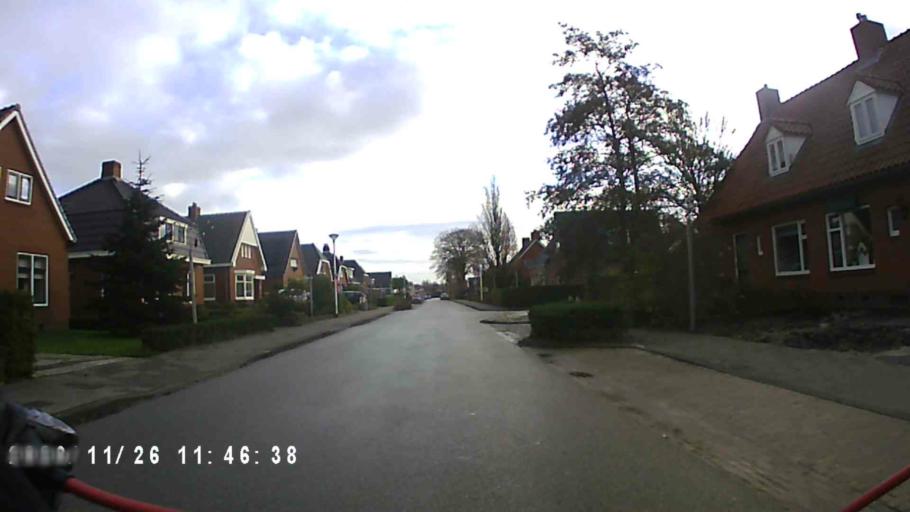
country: NL
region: Groningen
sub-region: Gemeente Bedum
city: Bedum
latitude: 53.3016
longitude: 6.5913
